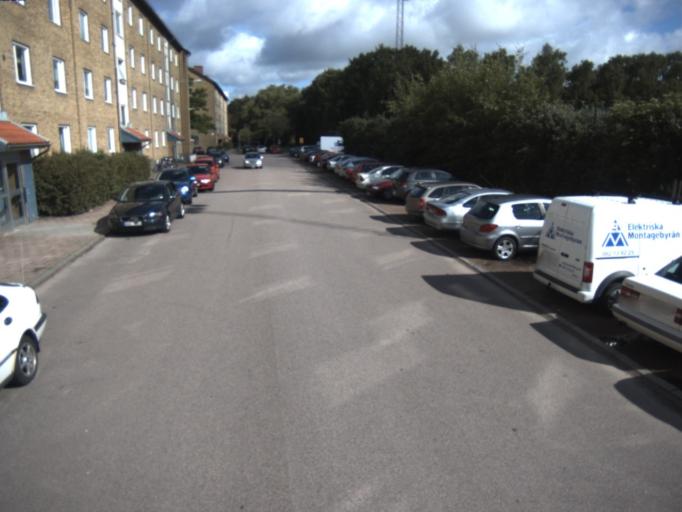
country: SE
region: Skane
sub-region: Helsingborg
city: Helsingborg
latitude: 56.0313
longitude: 12.7257
